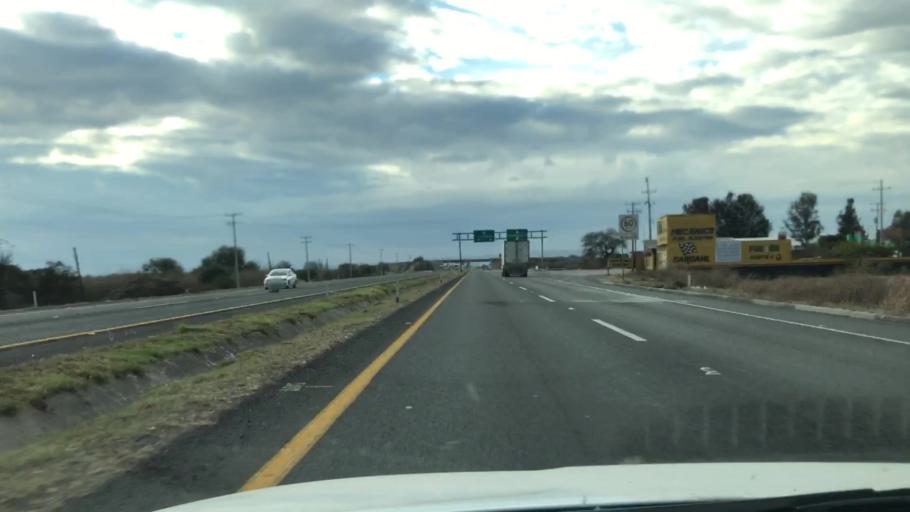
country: MX
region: Guanajuato
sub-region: Penjamo
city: Mezquite de Luna
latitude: 20.3790
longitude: -101.8573
